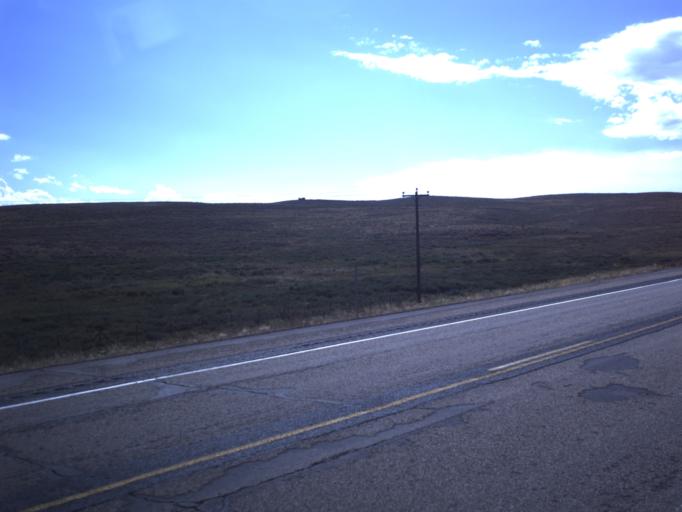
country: US
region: Utah
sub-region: Wasatch County
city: Heber
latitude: 40.1878
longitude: -111.0683
